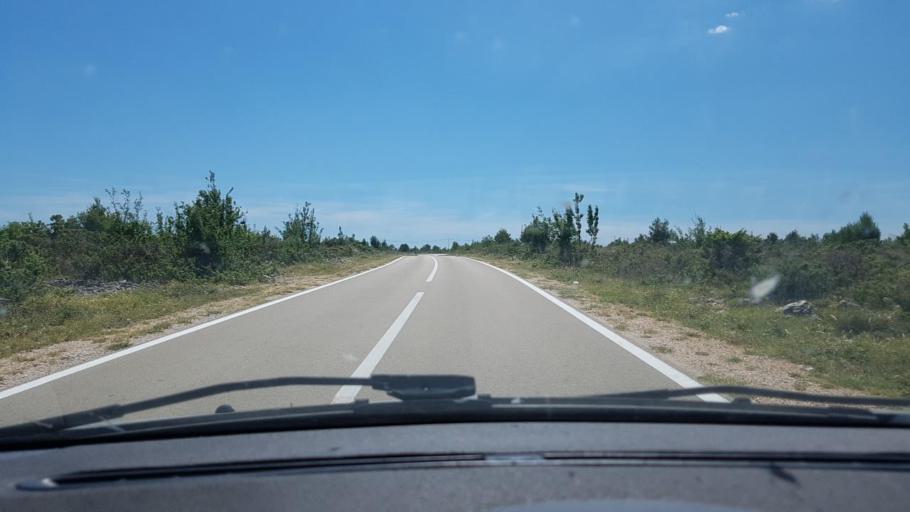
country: HR
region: Sibensko-Kniniska
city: Kistanje
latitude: 43.9143
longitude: 15.9334
